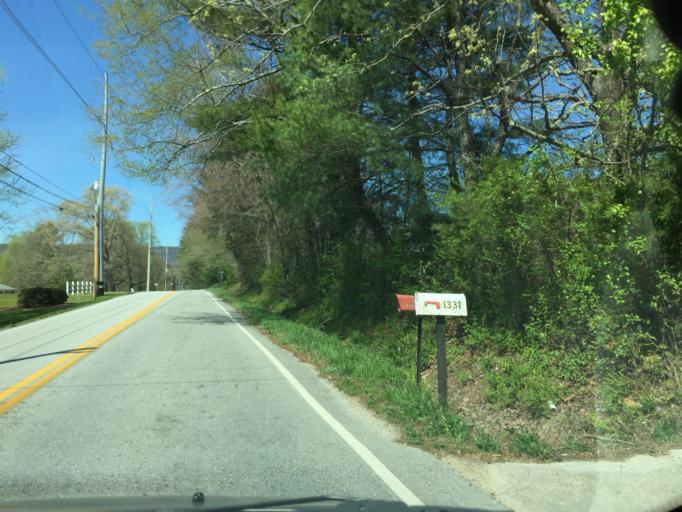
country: US
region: Tennessee
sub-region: Hamilton County
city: Middle Valley
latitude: 35.1993
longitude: -85.2028
